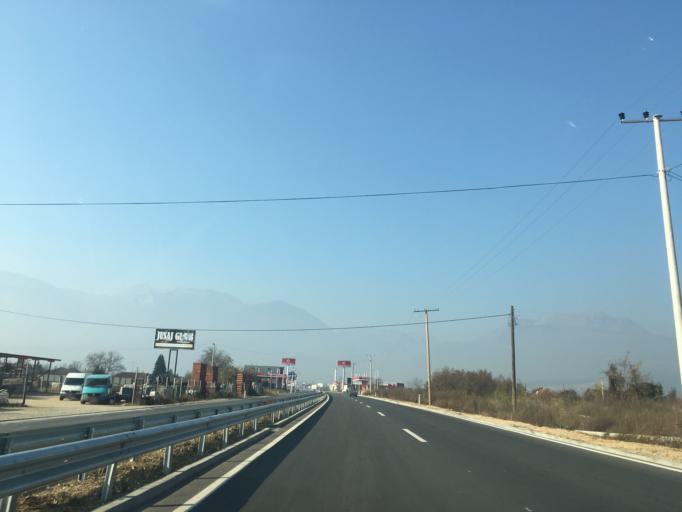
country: XK
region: Pec
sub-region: Komuna e Pejes
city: Peje
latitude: 42.6584
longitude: 20.3459
